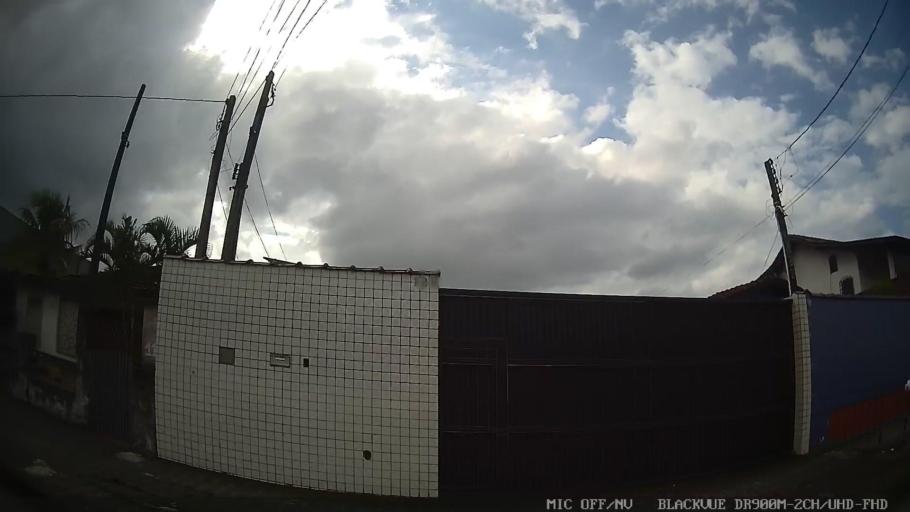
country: BR
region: Sao Paulo
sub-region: Guaruja
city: Guaruja
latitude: -23.9909
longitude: -46.2867
